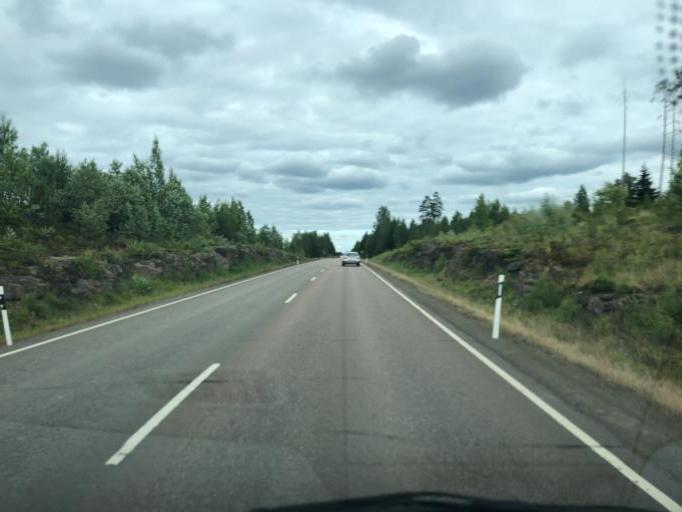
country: FI
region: Kymenlaakso
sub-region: Kouvola
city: Kouvola
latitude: 61.0503
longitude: 27.0278
